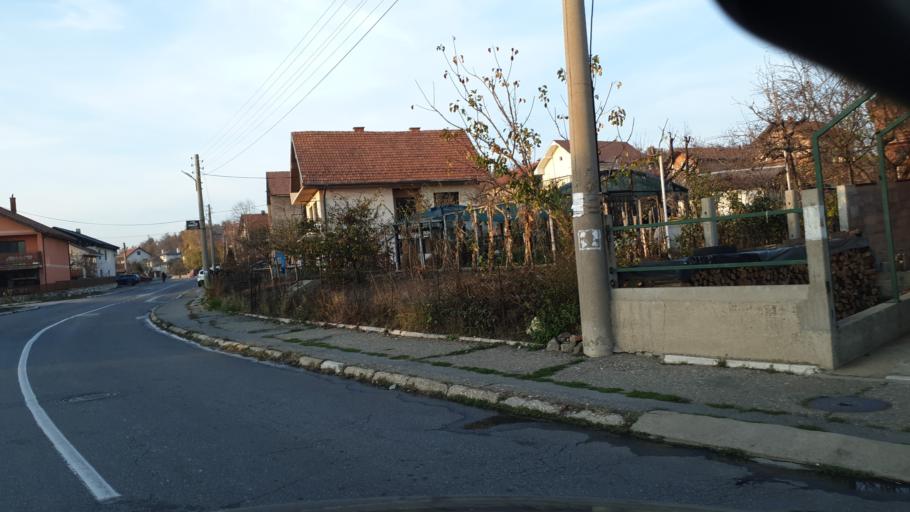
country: RS
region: Central Serbia
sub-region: Borski Okrug
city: Bor
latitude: 44.0572
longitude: 22.0834
